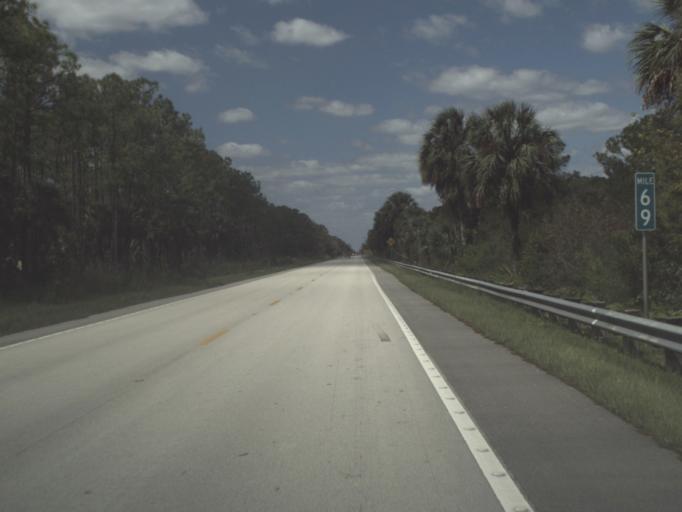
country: US
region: Florida
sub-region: Collier County
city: Marco
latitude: 25.8849
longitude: -81.2560
